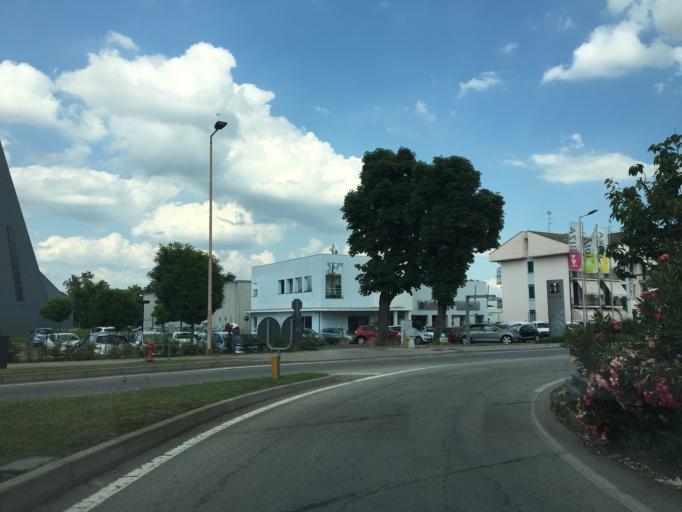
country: IT
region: Piedmont
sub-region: Provincia di Cuneo
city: Mussotto
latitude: 44.7149
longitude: 8.0139
